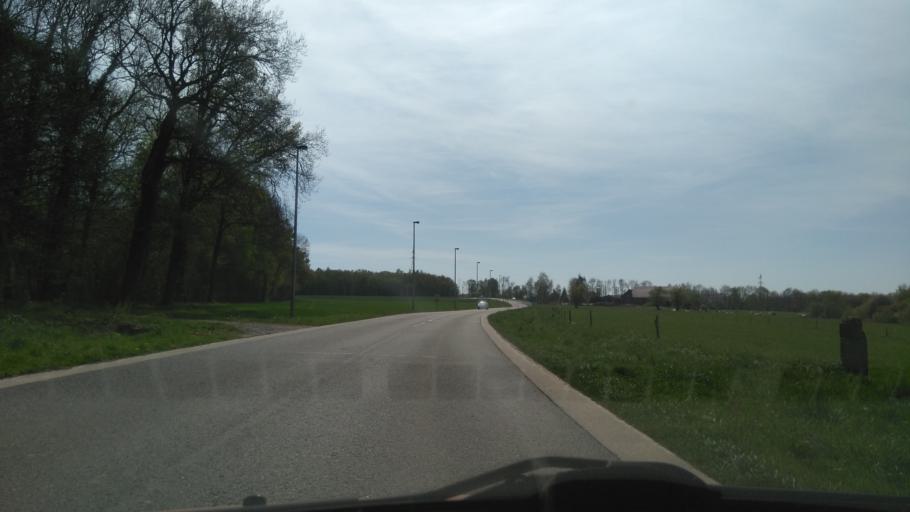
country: BE
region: Wallonia
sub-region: Province de Namur
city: Noville-les-Bois
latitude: 50.5337
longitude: 4.9800
